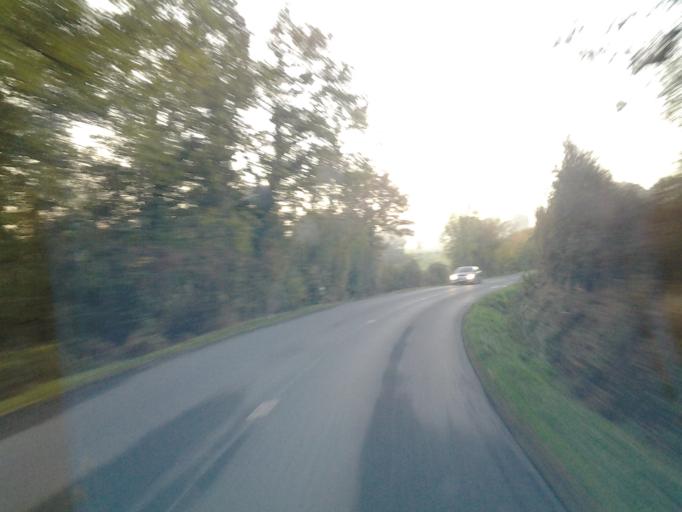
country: FR
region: Pays de la Loire
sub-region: Departement de la Vendee
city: Chateau-Guibert
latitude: 46.6295
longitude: -1.2330
